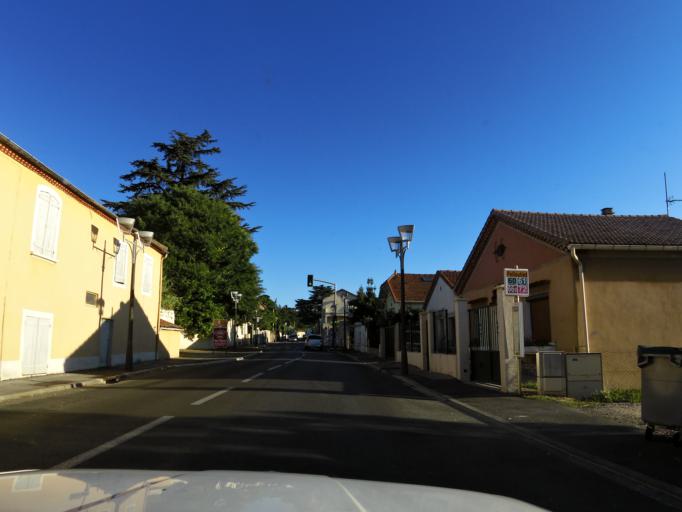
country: FR
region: Languedoc-Roussillon
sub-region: Departement du Gard
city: Ales
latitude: 44.1099
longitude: 4.0808
